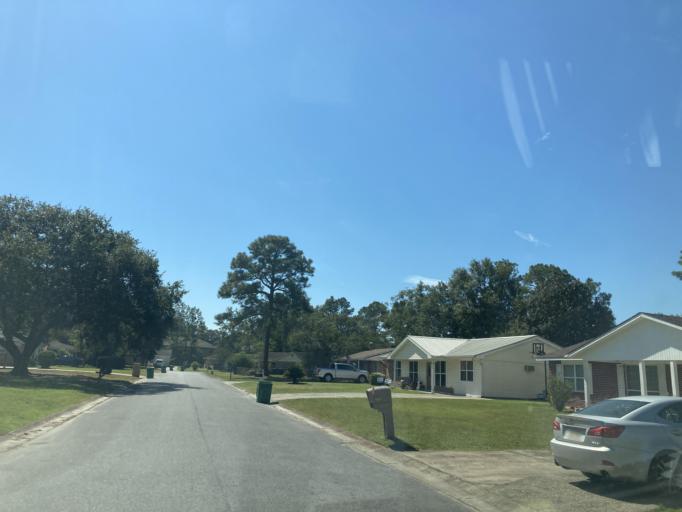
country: US
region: Mississippi
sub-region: Jackson County
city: Saint Martin
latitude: 30.4518
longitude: -88.8693
